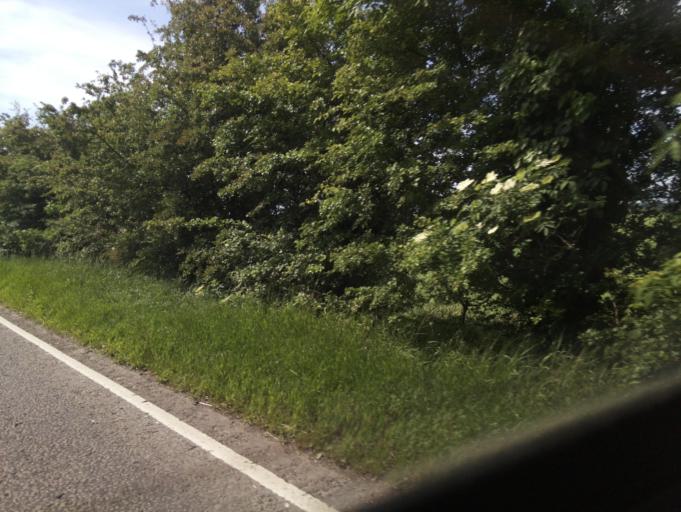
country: GB
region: England
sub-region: North Lincolnshire
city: Redbourne
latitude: 53.3880
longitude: -0.5472
